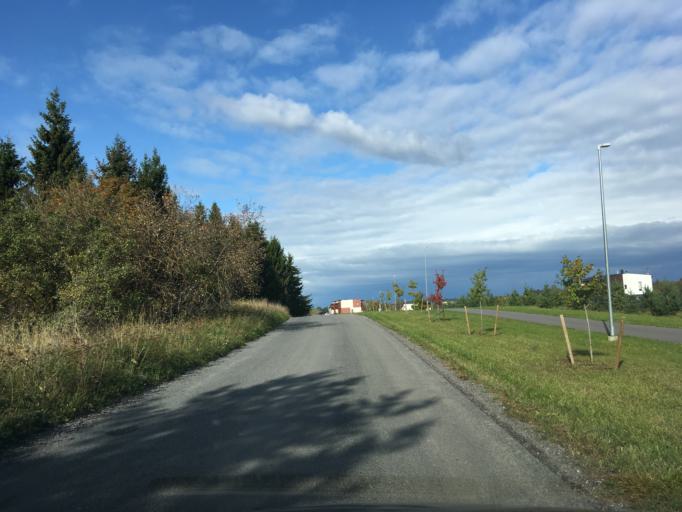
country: EE
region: Harju
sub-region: Saue vald
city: Laagri
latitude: 59.3435
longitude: 24.6481
